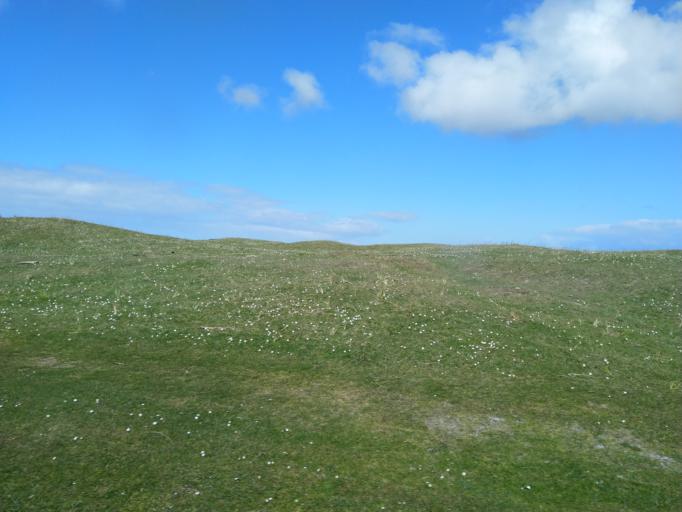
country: GB
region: Scotland
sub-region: Eilean Siar
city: Barra
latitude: 56.4779
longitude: -6.9766
